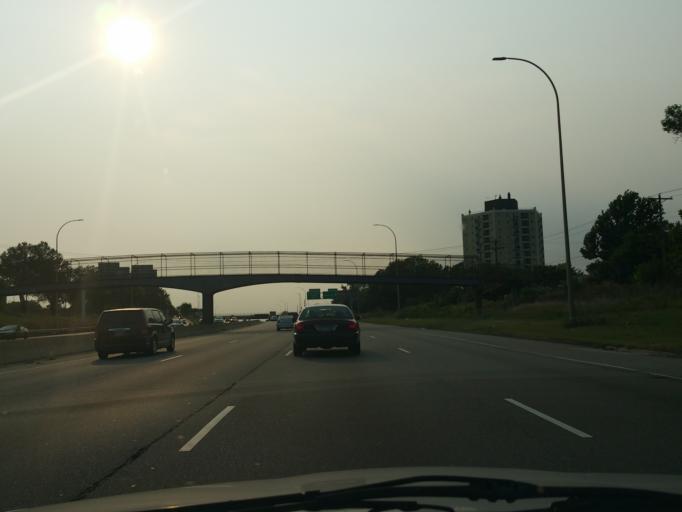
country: US
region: Minnesota
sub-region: Ramsey County
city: Saint Paul
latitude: 44.9517
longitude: -93.1194
